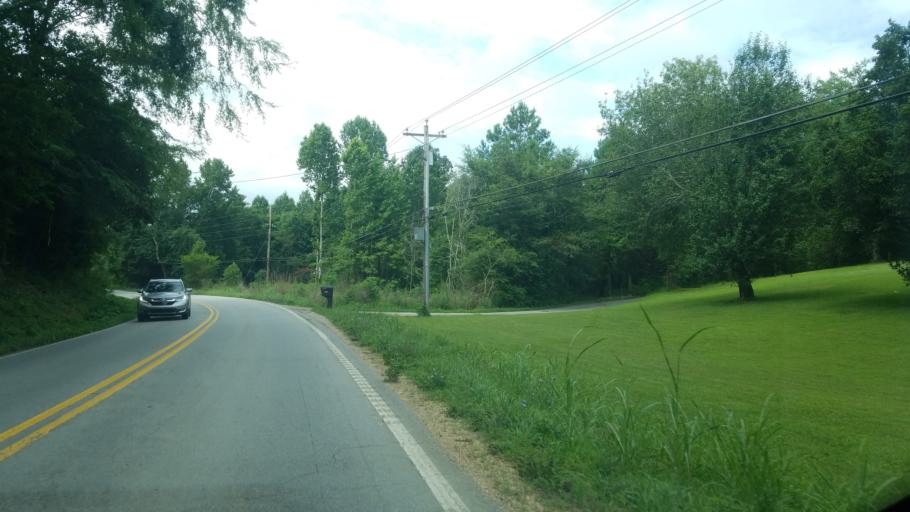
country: US
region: Tennessee
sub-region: Hamilton County
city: Lakesite
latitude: 35.2003
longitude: -85.0701
